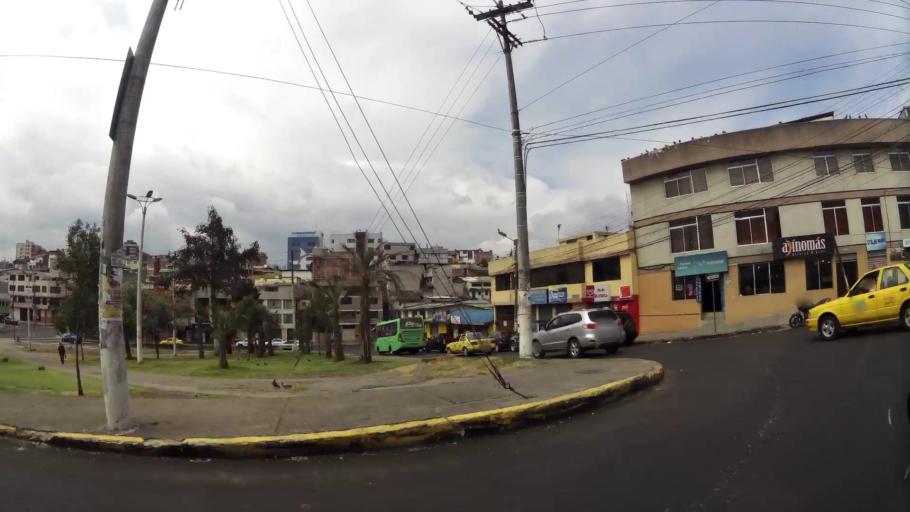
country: EC
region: Pichincha
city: Quito
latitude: -0.2133
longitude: -78.4847
